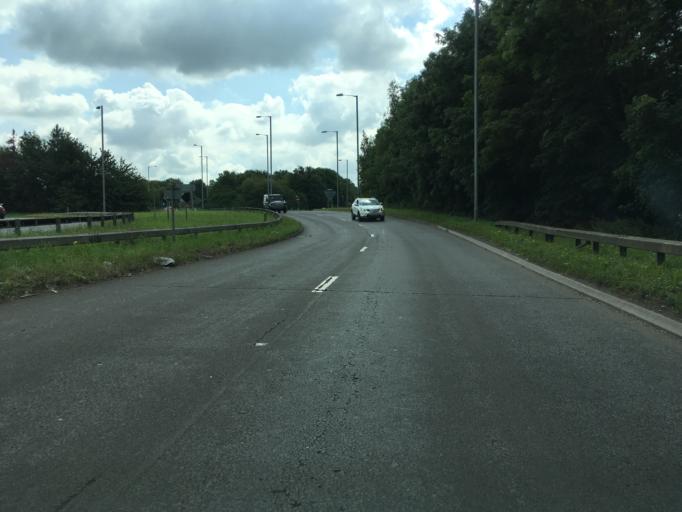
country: GB
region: England
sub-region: Gloucestershire
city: Barnwood
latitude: 51.8615
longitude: -2.1859
